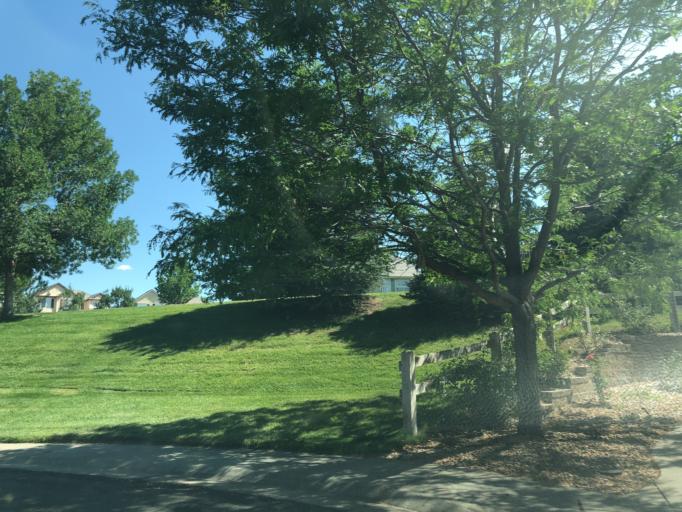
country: US
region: Colorado
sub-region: Arapahoe County
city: Dove Valley
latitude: 39.6085
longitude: -104.7866
